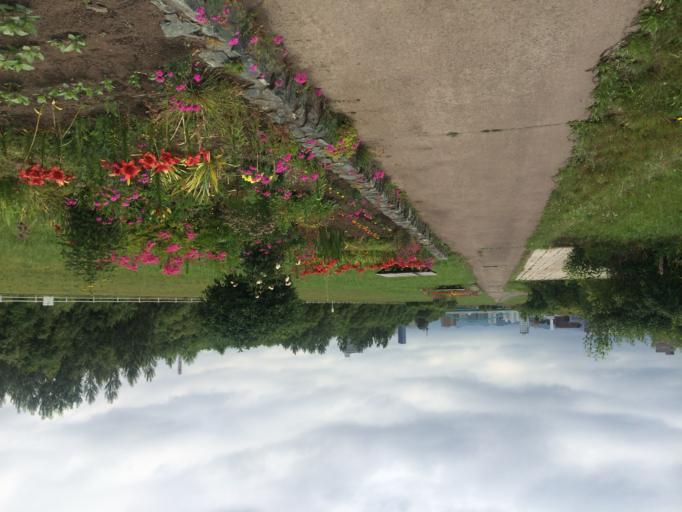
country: JP
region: Hokkaido
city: Sapporo
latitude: 43.0663
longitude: 141.3862
